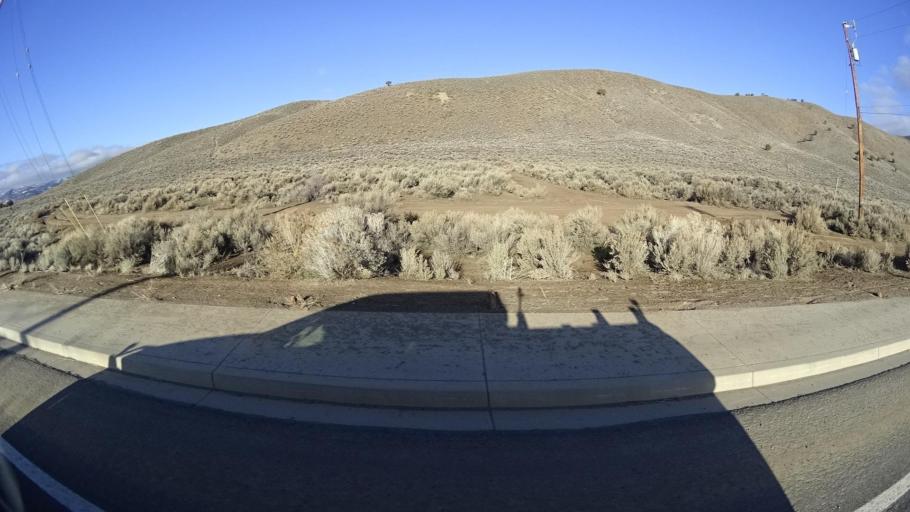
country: US
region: Nevada
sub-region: Washoe County
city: Cold Springs
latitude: 39.6866
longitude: -119.9785
